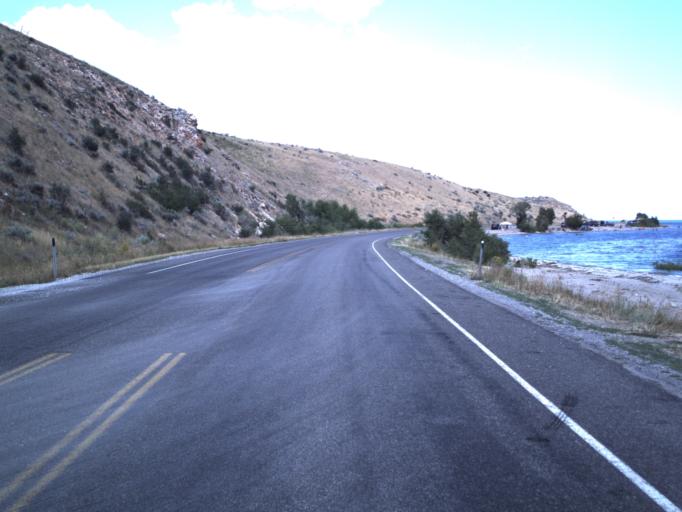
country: US
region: Utah
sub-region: Rich County
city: Randolph
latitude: 41.8591
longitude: -111.3651
